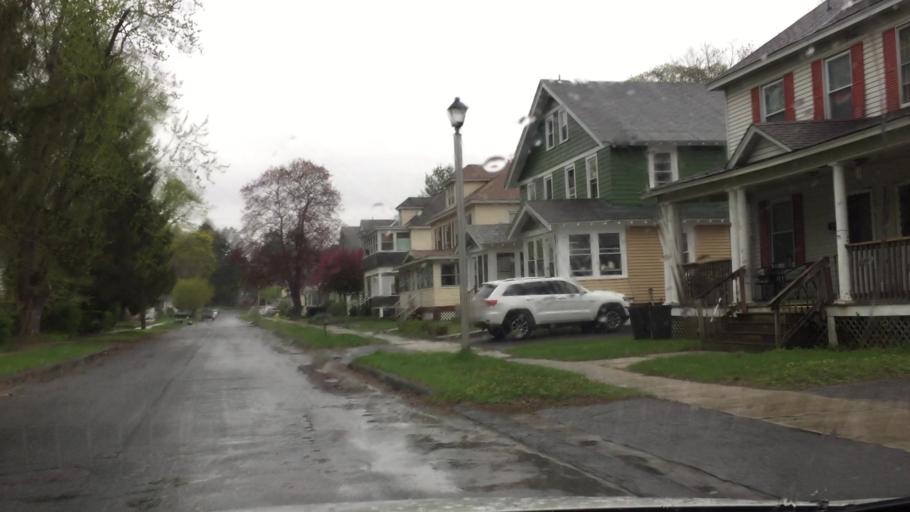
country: US
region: Massachusetts
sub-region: Berkshire County
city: Pittsfield
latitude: 42.4392
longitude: -73.2603
